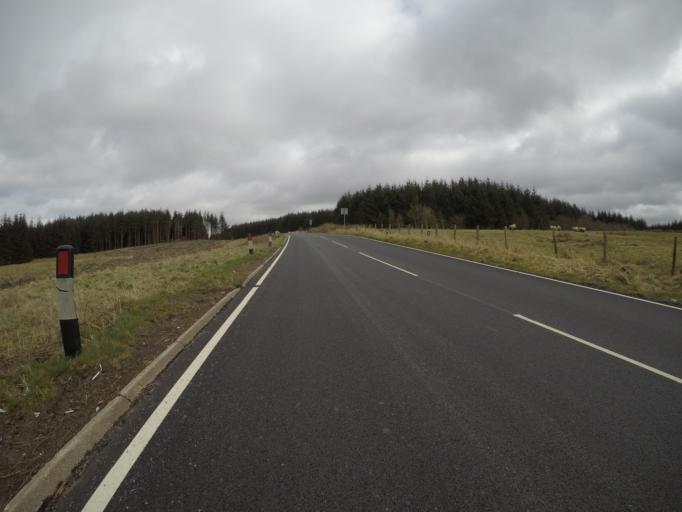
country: GB
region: Scotland
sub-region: East Renfrewshire
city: Newton Mearns
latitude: 55.7031
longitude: -4.3739
